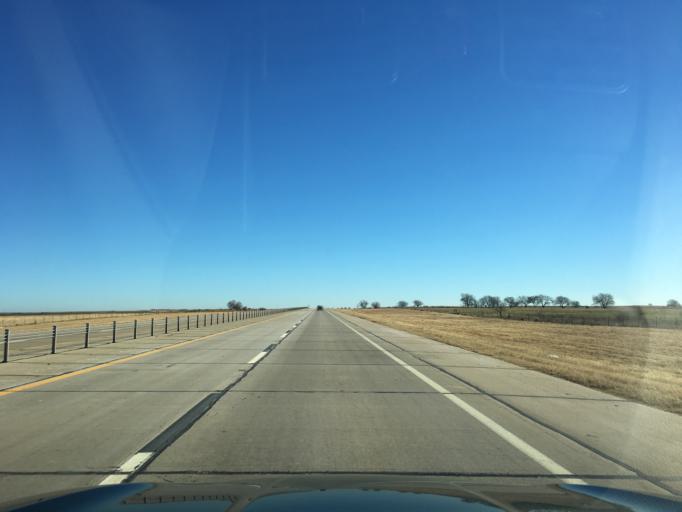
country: US
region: Oklahoma
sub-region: Noble County
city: Perry
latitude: 36.4007
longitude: -97.2449
